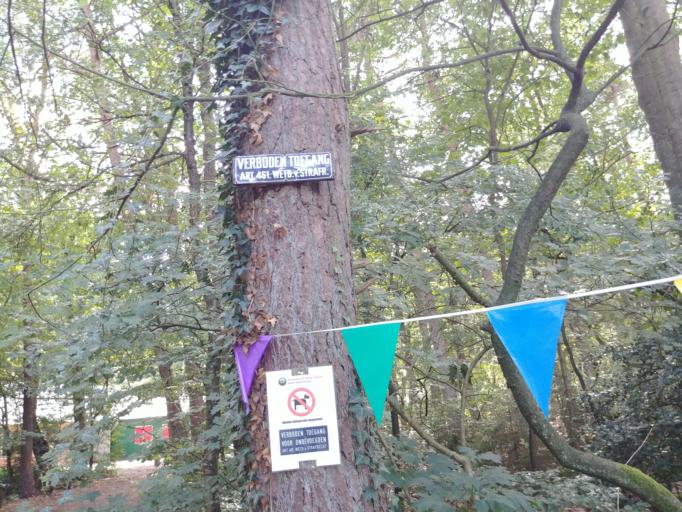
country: NL
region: Utrecht
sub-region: Gemeente Utrechtse Heuvelrug
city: Maarn
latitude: 52.0602
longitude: 5.3723
